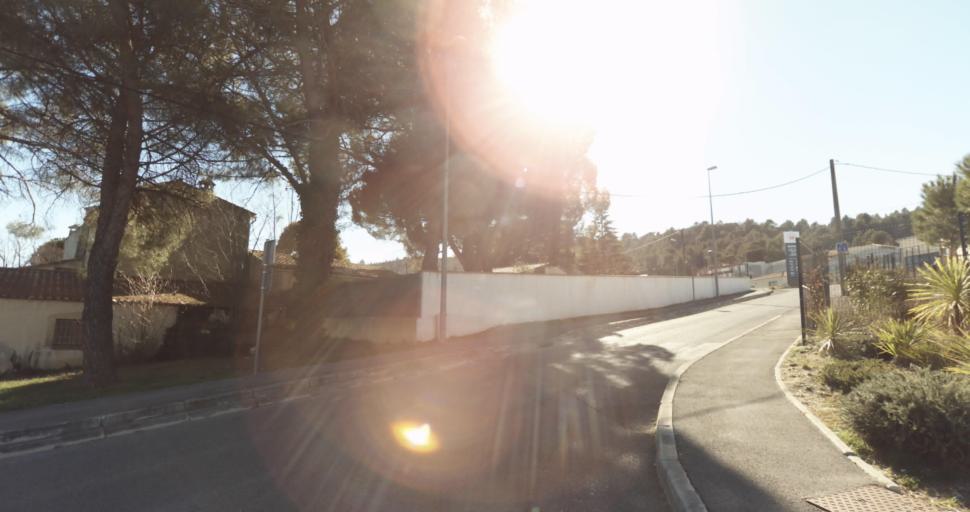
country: FR
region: Provence-Alpes-Cote d'Azur
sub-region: Departement des Bouches-du-Rhone
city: Cadolive
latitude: 43.3919
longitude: 5.5523
